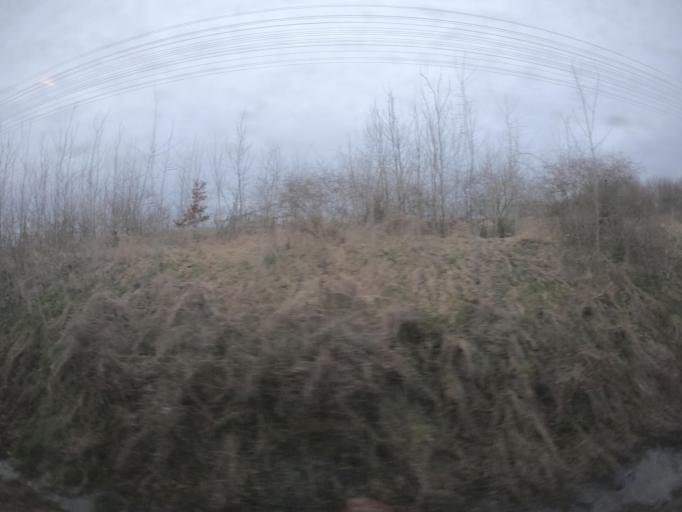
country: PL
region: West Pomeranian Voivodeship
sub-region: Powiat szczecinecki
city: Szczecinek
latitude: 53.6814
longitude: 16.6841
